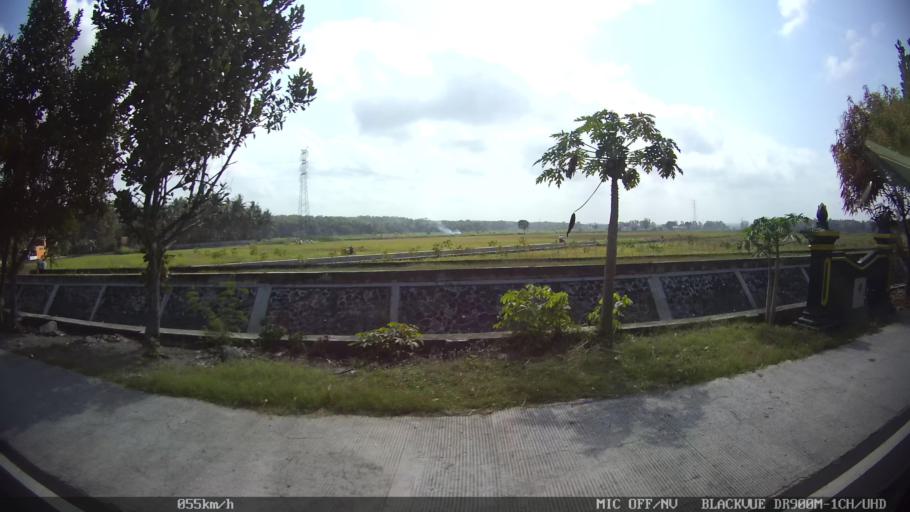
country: ID
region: Daerah Istimewa Yogyakarta
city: Srandakan
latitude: -7.9032
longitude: 110.1685
